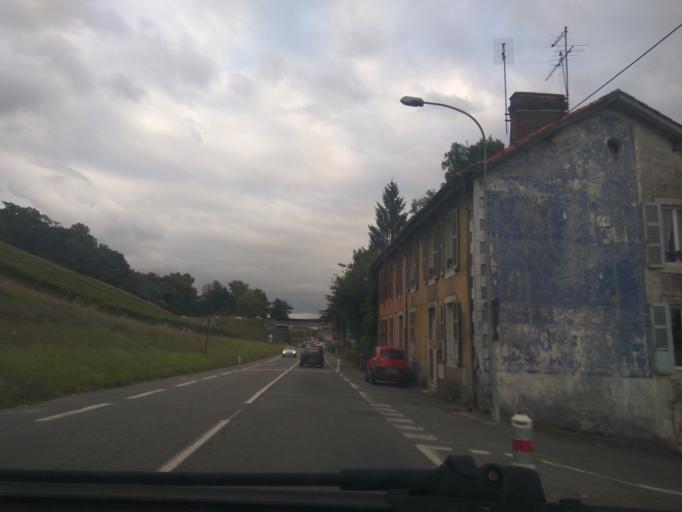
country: FR
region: Aquitaine
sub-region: Departement des Pyrenees-Atlantiques
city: Bizanos
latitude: 43.2859
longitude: -0.3486
